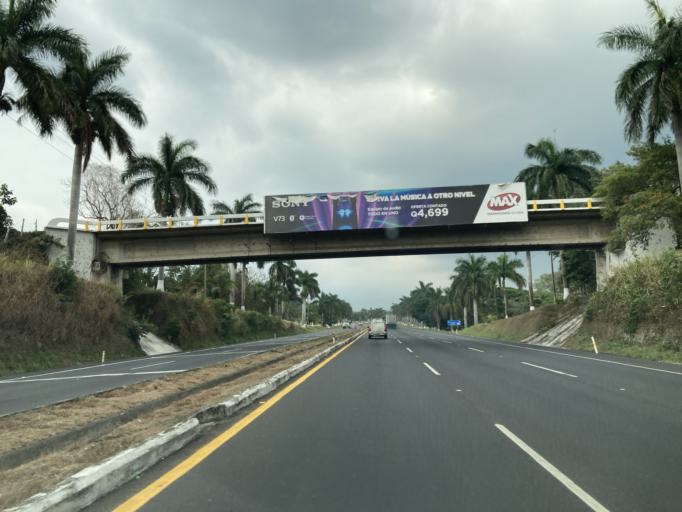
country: GT
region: Escuintla
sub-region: Municipio de Escuintla
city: Escuintla
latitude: 14.3487
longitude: -90.7864
